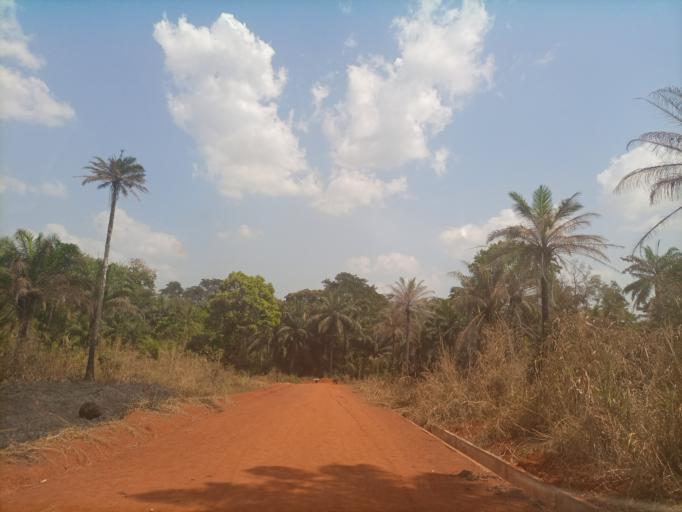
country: NG
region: Enugu
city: Obolo-Eke (1)
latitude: 6.8641
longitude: 7.6604
